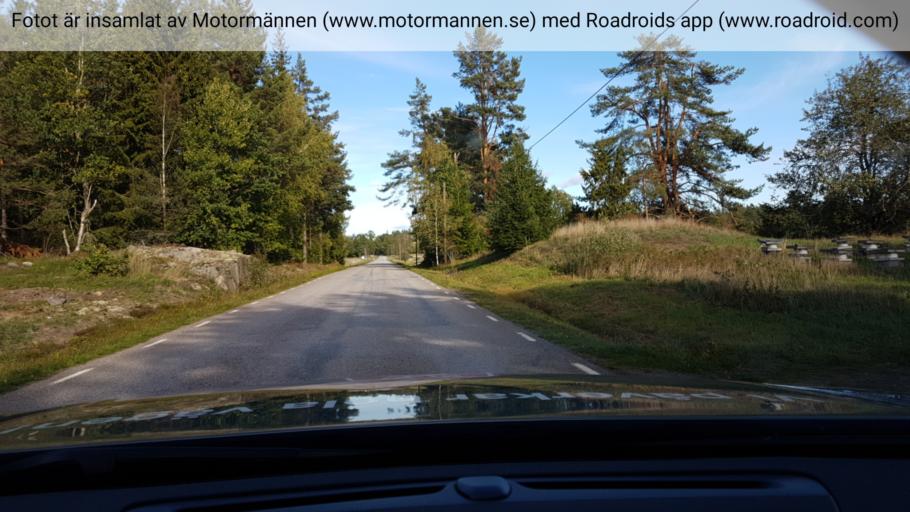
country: SE
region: OEstergoetland
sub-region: Valdemarsviks Kommun
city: Valdemarsvik
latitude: 58.0493
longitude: 16.6088
